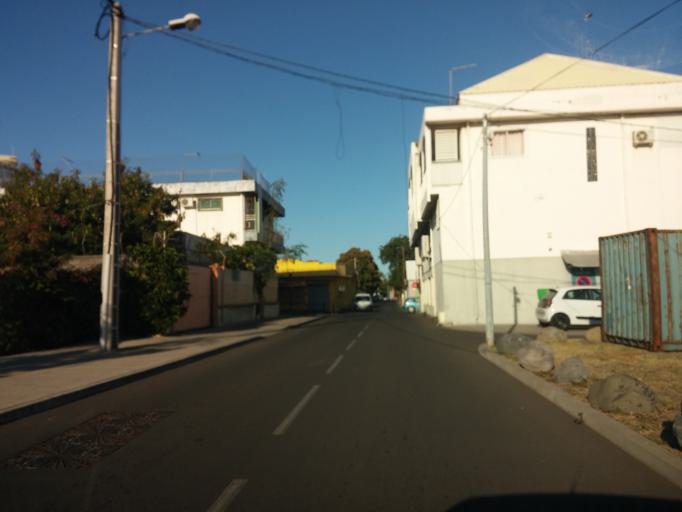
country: RE
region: Reunion
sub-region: Reunion
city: Le Port
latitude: -20.9384
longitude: 55.2943
